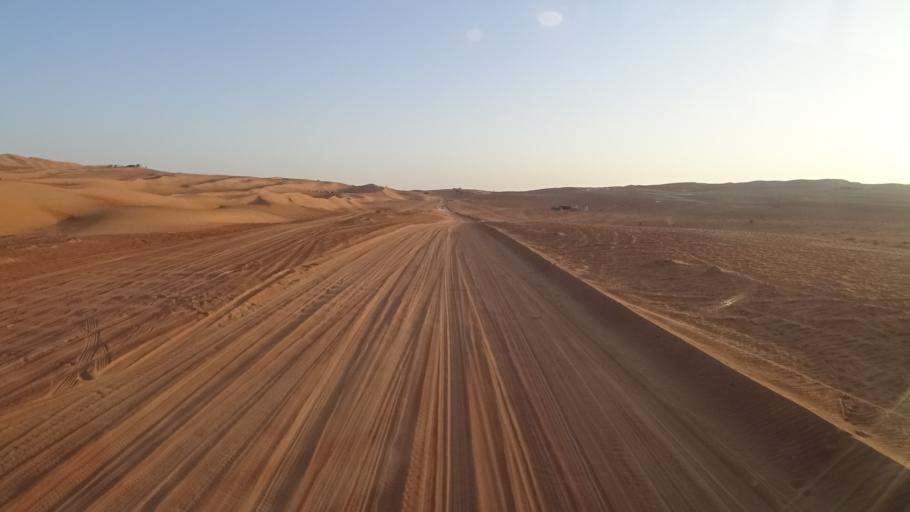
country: OM
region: Ash Sharqiyah
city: Badiyah
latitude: 22.4872
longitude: 58.7292
